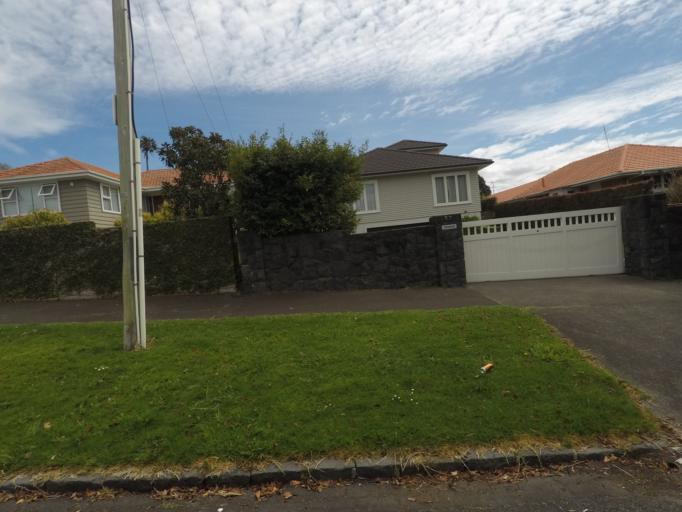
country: NZ
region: Auckland
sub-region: Auckland
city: Auckland
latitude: -36.8850
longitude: 174.7214
